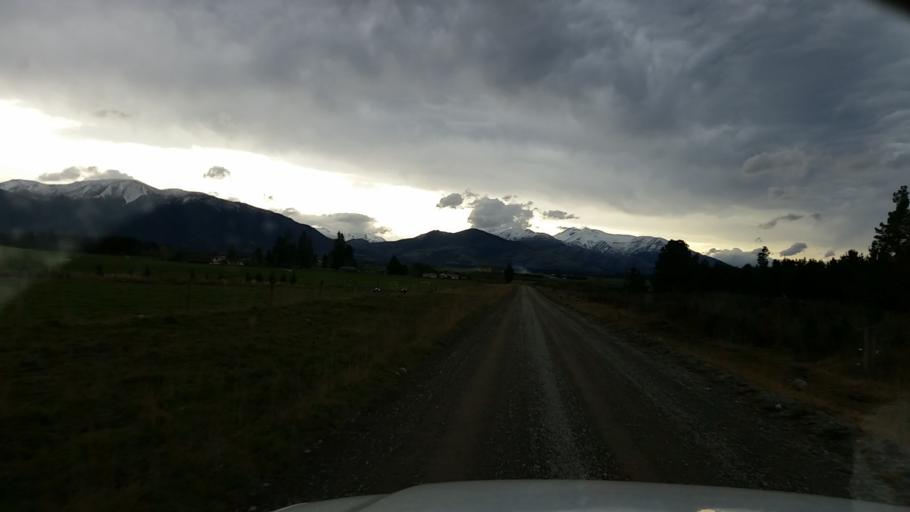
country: NZ
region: Canterbury
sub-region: Ashburton District
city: Methven
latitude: -43.7010
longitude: 171.4605
